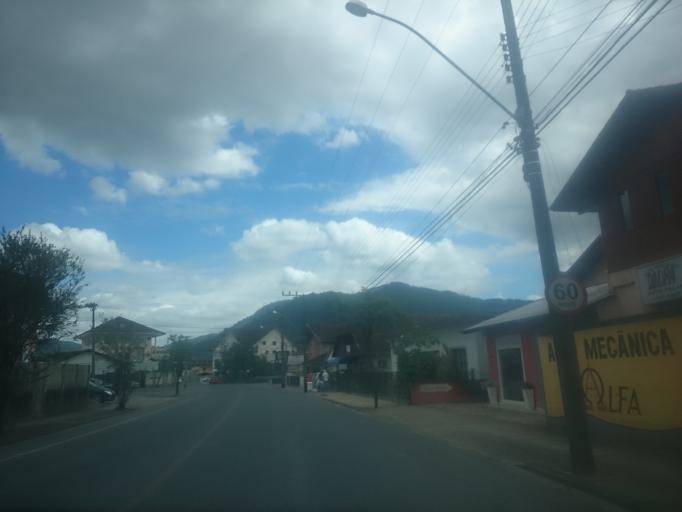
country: BR
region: Santa Catarina
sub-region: Pomerode
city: Pomerode
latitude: -26.7236
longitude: -49.1697
